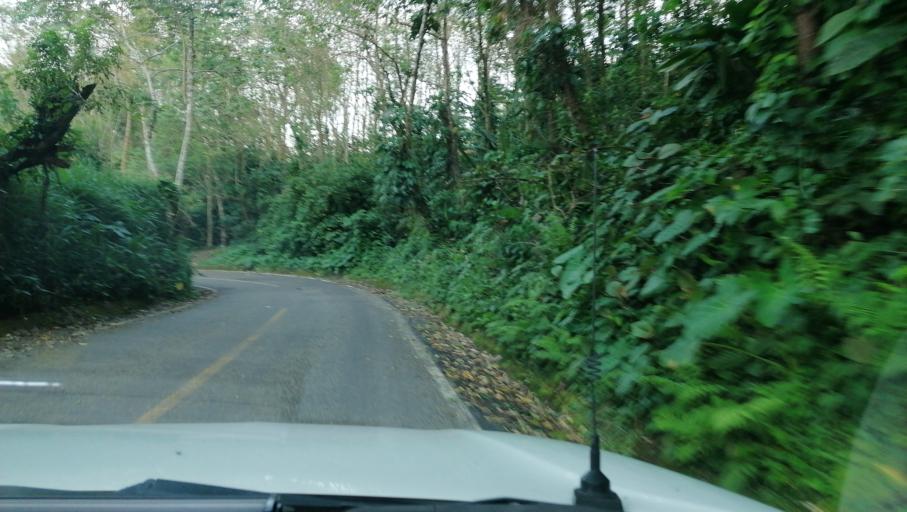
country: MX
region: Chiapas
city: Pichucalco
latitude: 17.5108
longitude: -93.2097
